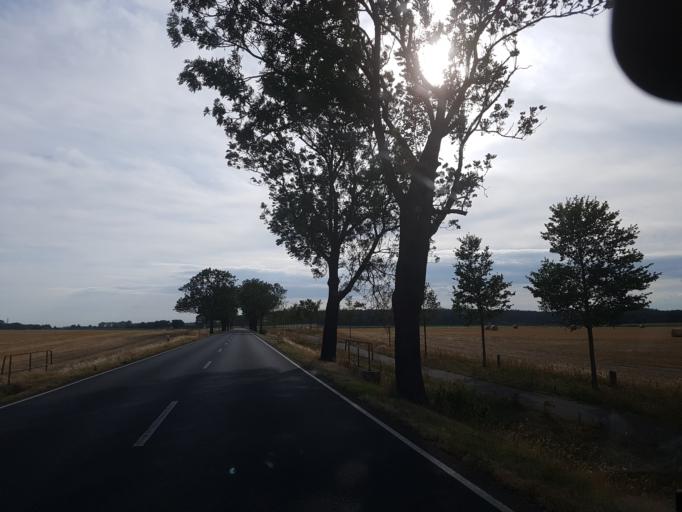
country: DE
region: Brandenburg
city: Schlieben
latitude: 51.7258
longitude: 13.3077
